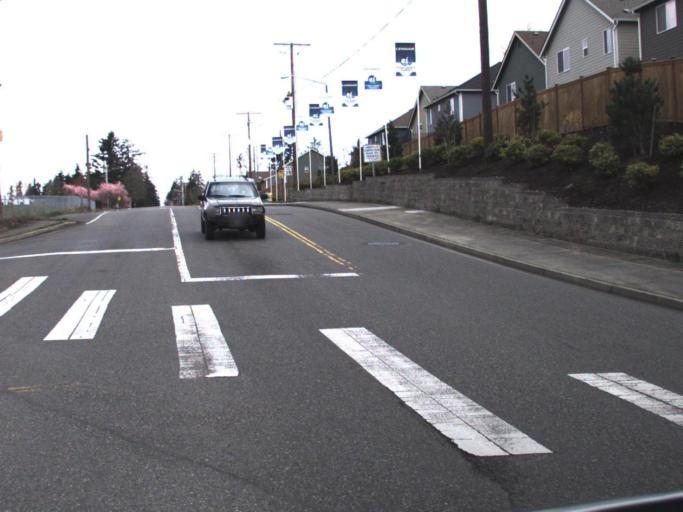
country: US
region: Washington
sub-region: Pierce County
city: Edgewood
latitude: 47.2621
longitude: -122.2980
